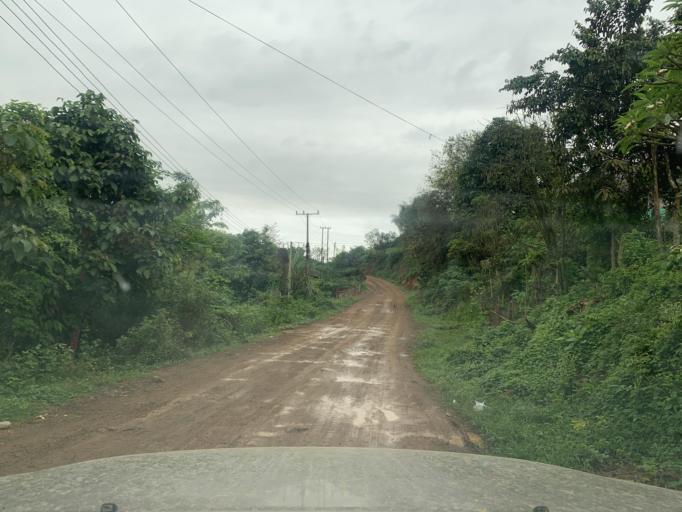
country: LA
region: Vientiane
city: Muang Sanakham
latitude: 18.4092
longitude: 101.4910
